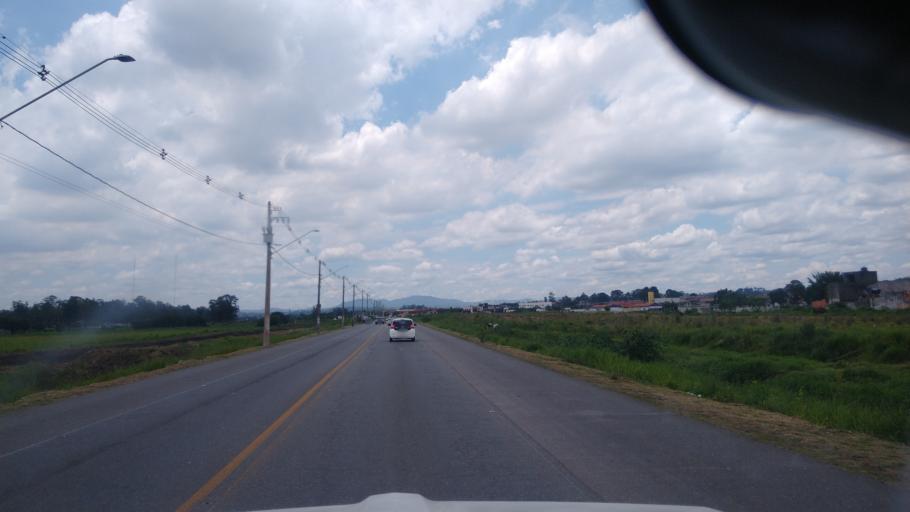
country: BR
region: Sao Paulo
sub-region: Itaquaquecetuba
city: Itaquaquecetuba
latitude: -23.5009
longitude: -46.3220
